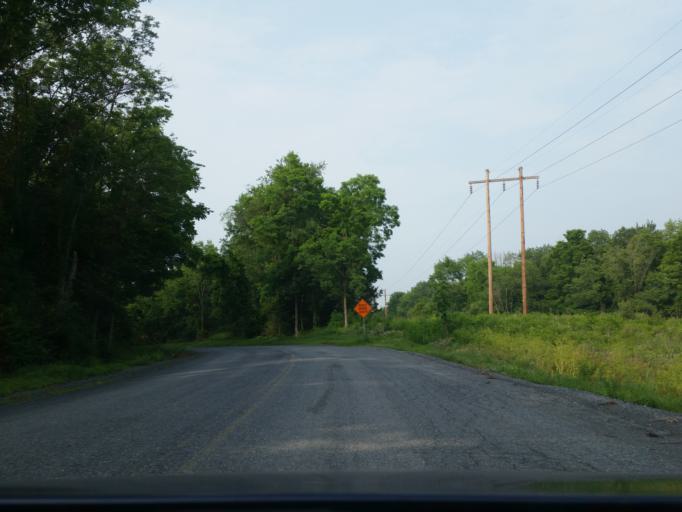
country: US
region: Pennsylvania
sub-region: Lebanon County
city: Jonestown
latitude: 40.4168
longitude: -76.5806
